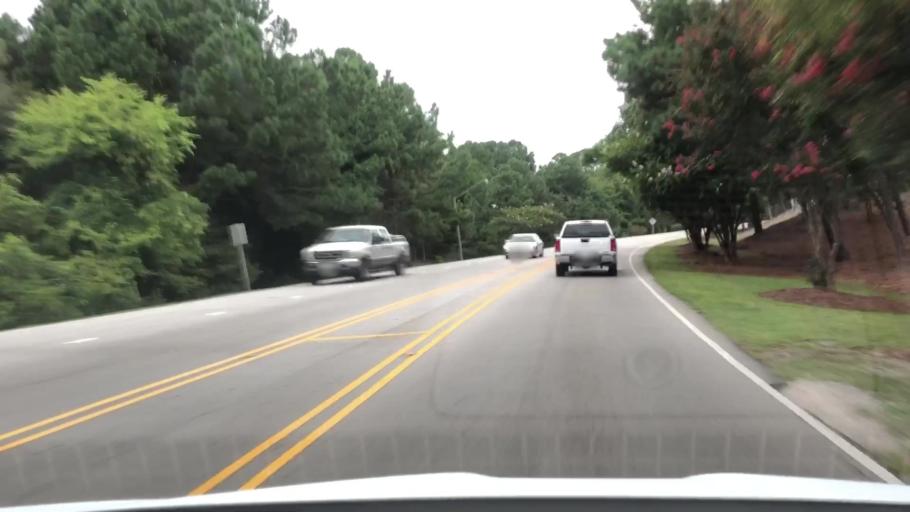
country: US
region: North Carolina
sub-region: Carteret County
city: Cedar Point
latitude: 34.6616
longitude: -77.0607
